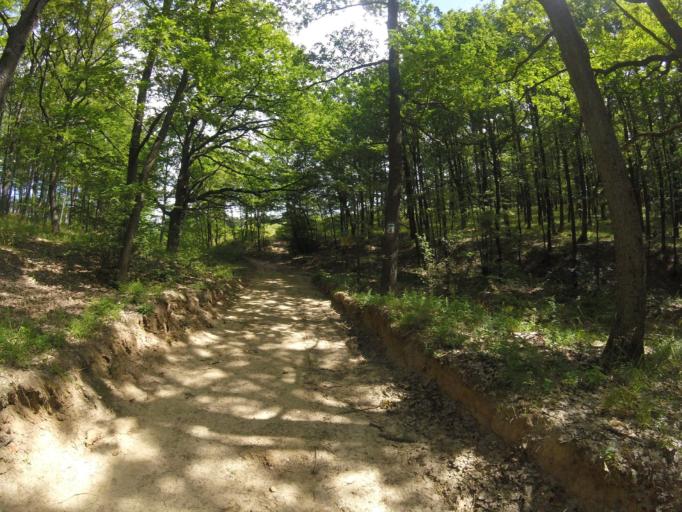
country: HU
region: Nograd
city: Romhany
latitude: 47.8913
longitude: 19.2471
